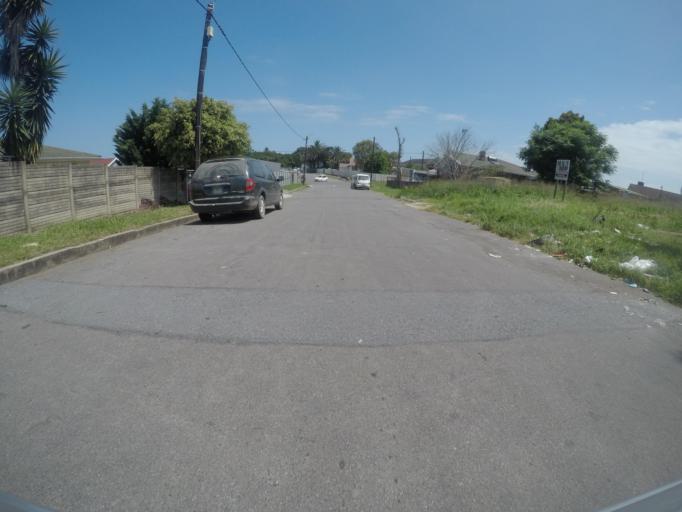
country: ZA
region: Eastern Cape
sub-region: Buffalo City Metropolitan Municipality
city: East London
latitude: -32.9728
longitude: 27.8687
